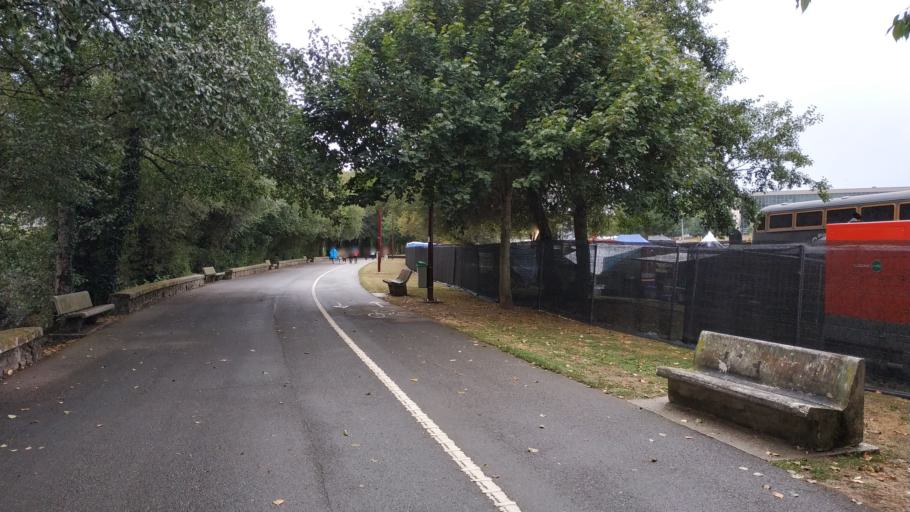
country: ES
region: Galicia
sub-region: Provincia de Lugo
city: Lugo
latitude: 43.0019
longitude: -7.5662
